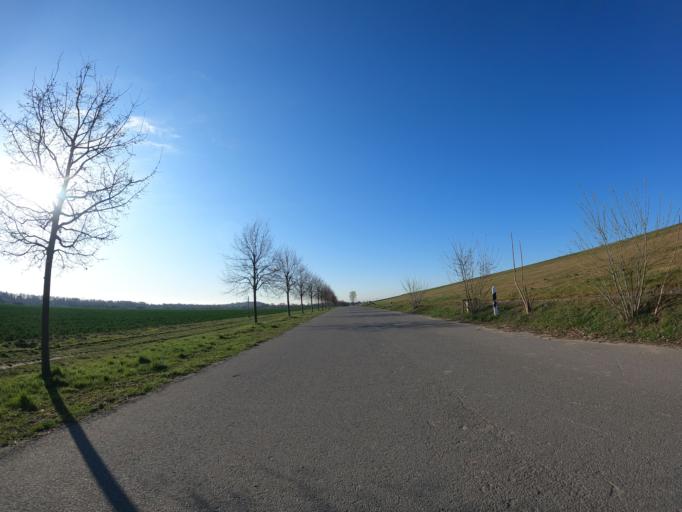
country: DE
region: Berlin
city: Gropiusstadt
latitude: 52.4137
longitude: 13.4629
